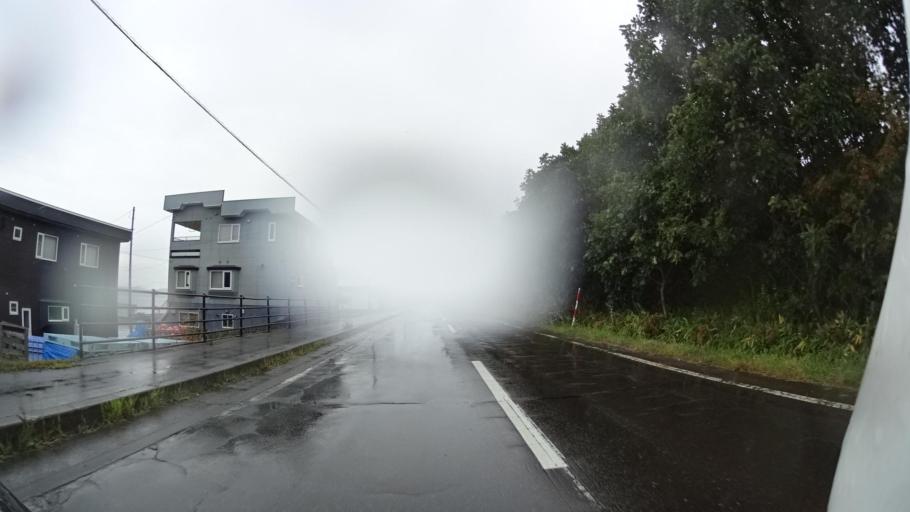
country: JP
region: Hokkaido
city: Mombetsu
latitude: 44.3324
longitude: 143.4900
